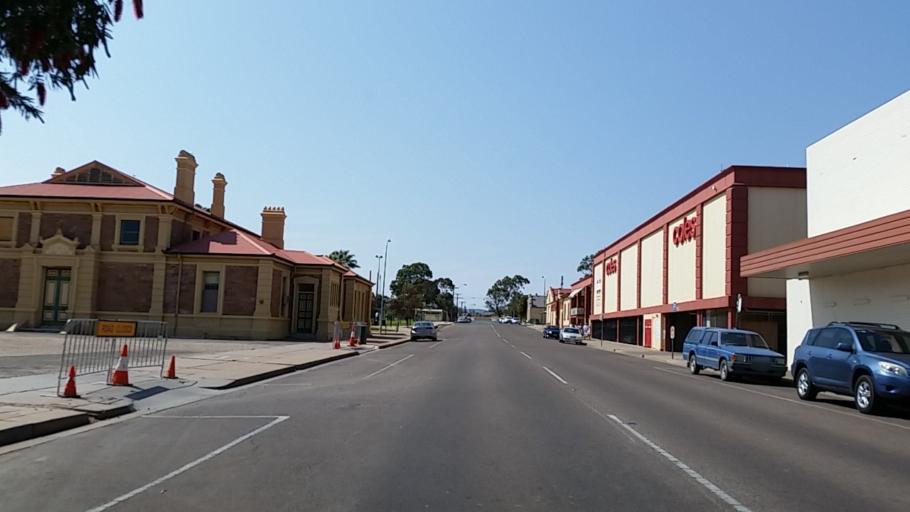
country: AU
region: South Australia
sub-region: Port Augusta
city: Port Augusta West
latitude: -32.4926
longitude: 137.7631
